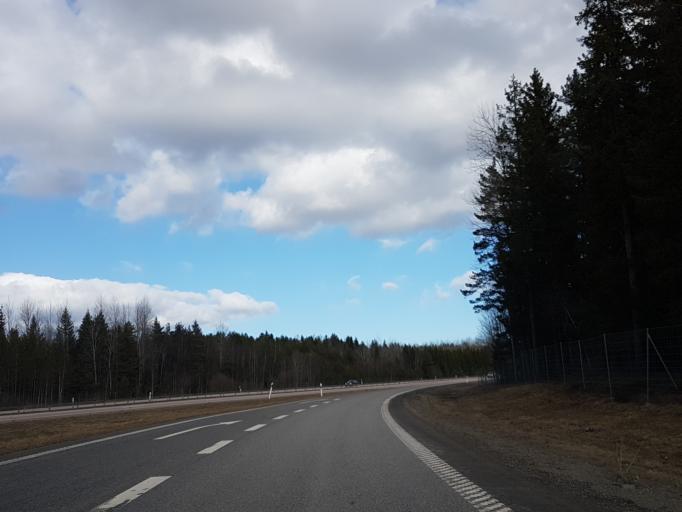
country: SE
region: Stockholm
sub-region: Norrtalje Kommun
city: Norrtalje
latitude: 59.7333
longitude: 18.5717
